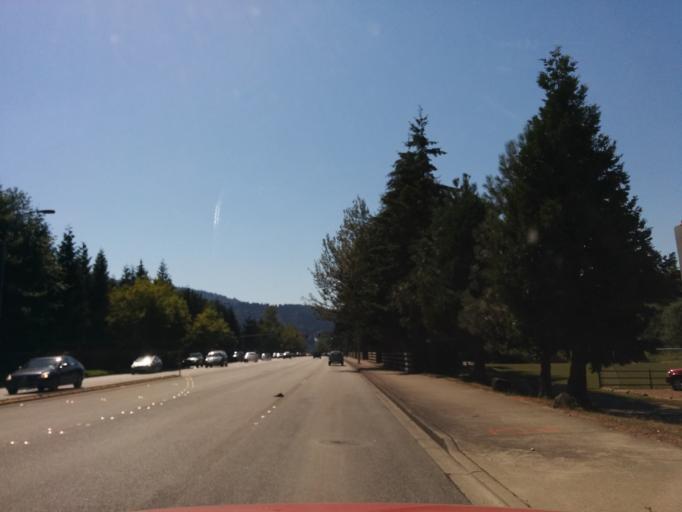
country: US
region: Washington
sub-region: King County
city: Issaquah
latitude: 47.5521
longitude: -122.0520
